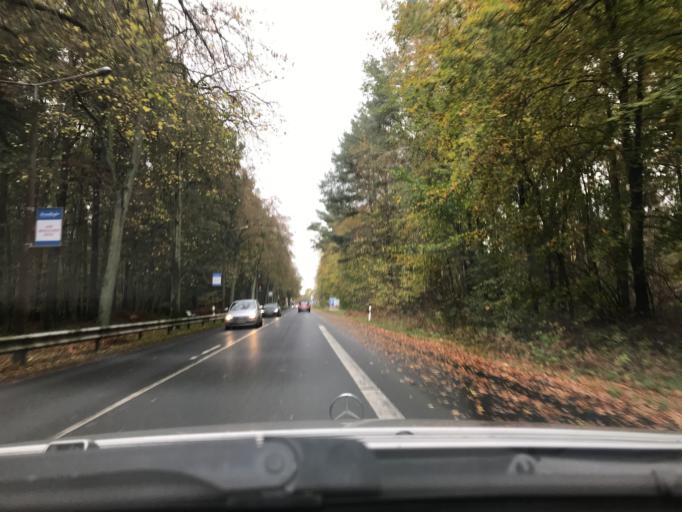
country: PL
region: West Pomeranian Voivodeship
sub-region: Swinoujscie
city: Swinoujscie
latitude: 53.9258
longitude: 14.2093
